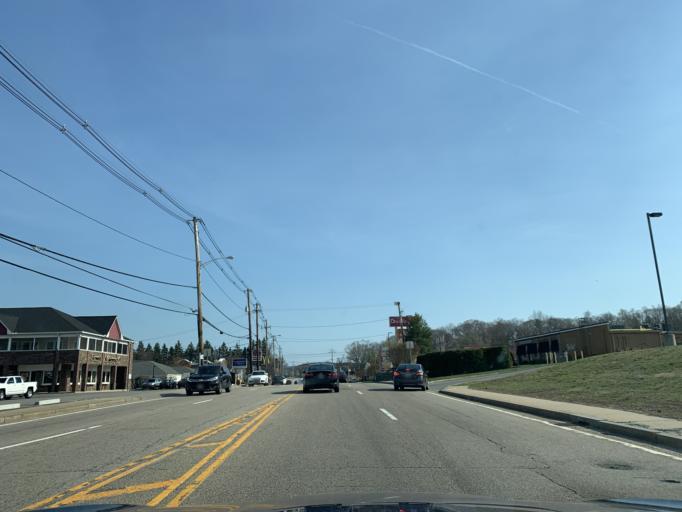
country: US
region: Rhode Island
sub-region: Providence County
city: Johnston
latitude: 41.8163
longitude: -71.4966
